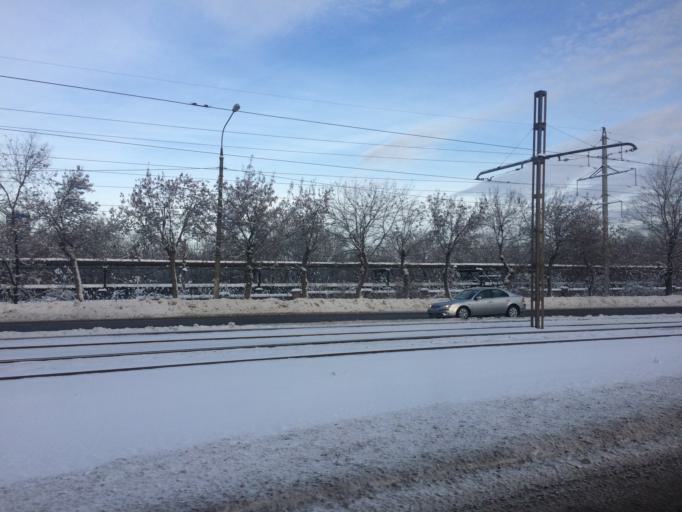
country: RU
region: Chelyabinsk
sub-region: Gorod Magnitogorsk
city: Magnitogorsk
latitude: 53.3961
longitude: 59.0291
